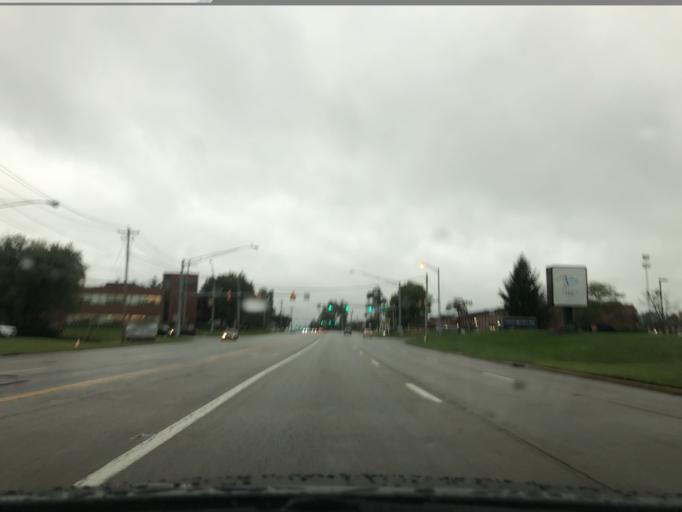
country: US
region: Ohio
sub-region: Hamilton County
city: Highpoint
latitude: 39.2749
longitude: -84.3747
